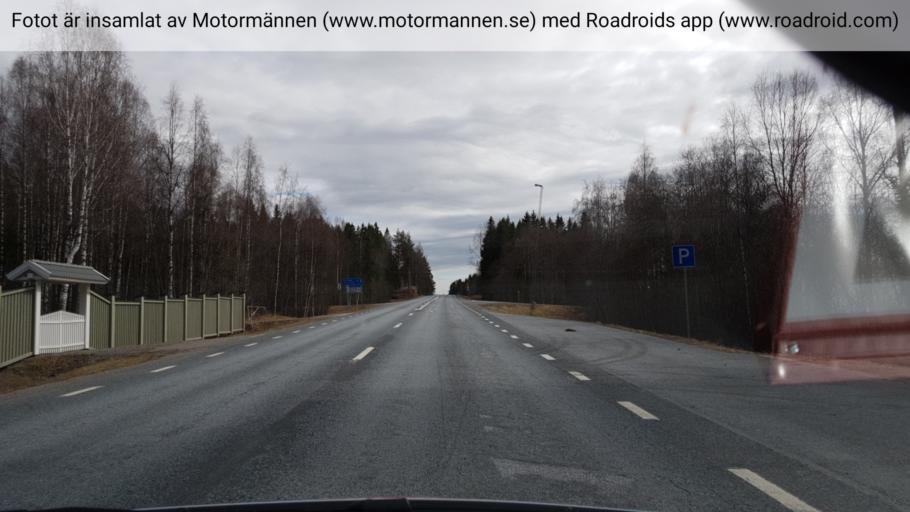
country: SE
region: Vaesternorrland
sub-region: Solleftea Kommun
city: Solleftea
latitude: 63.3920
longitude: 16.9788
